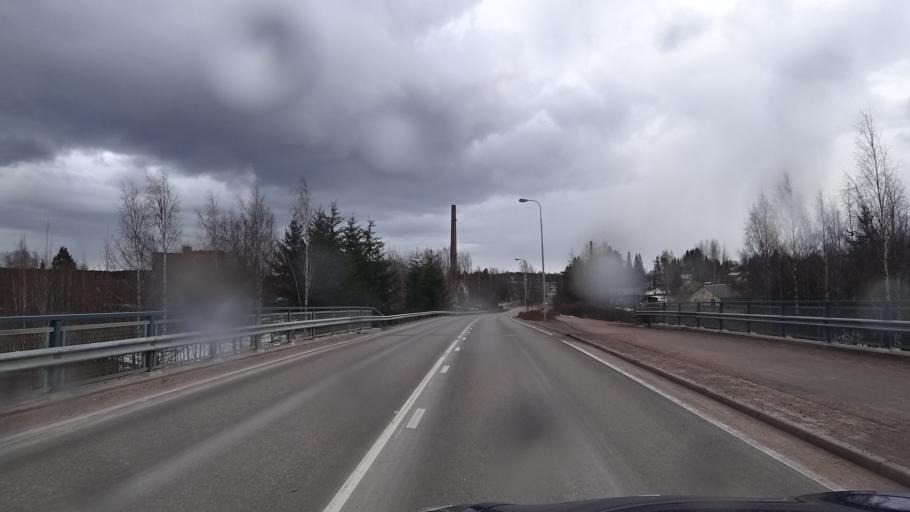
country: FI
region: Kymenlaakso
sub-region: Kotka-Hamina
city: Karhula
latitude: 60.5369
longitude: 26.9045
